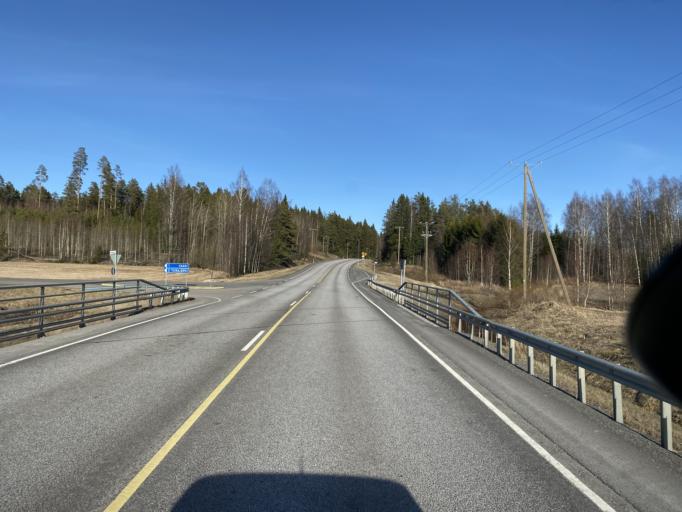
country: FI
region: Satakunta
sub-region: Rauma
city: Kiukainen
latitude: 61.1306
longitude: 21.9880
